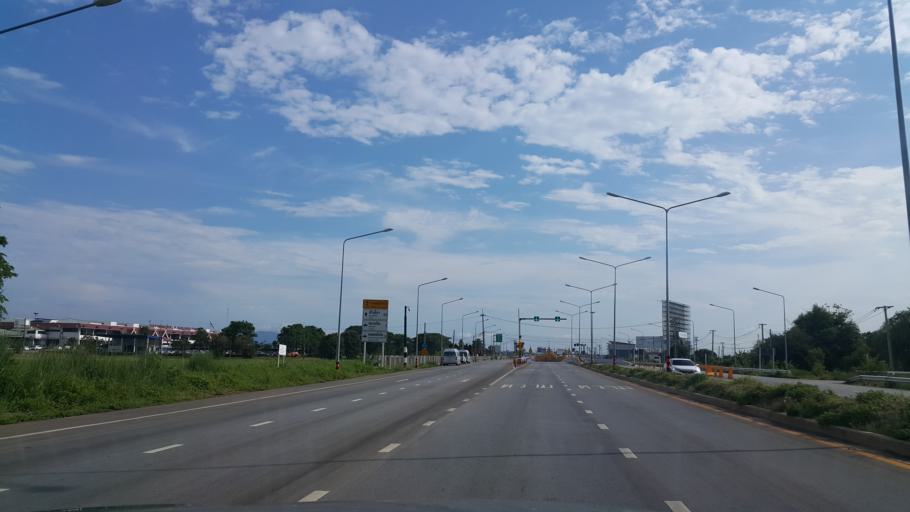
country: TH
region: Chiang Rai
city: Chiang Rai
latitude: 19.9587
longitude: 99.8793
